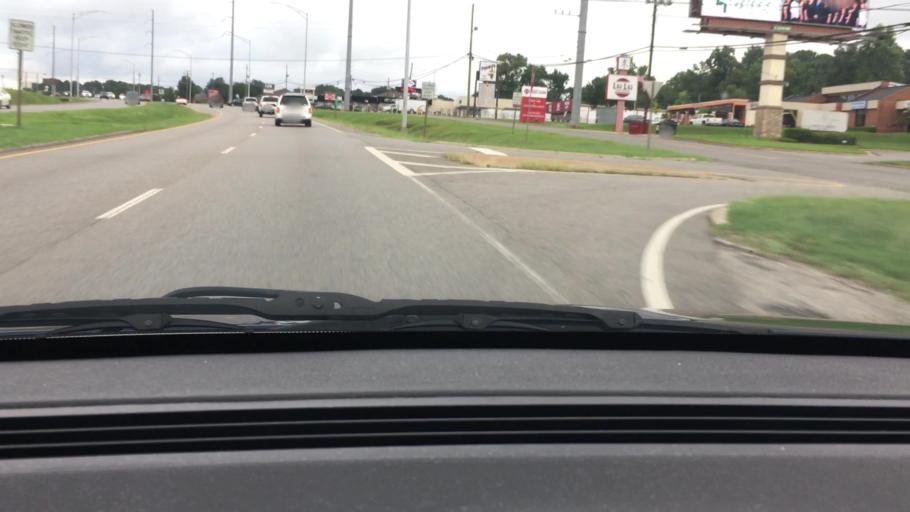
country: US
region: Alabama
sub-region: Tuscaloosa County
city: Tuscaloosa
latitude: 33.2290
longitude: -87.5335
